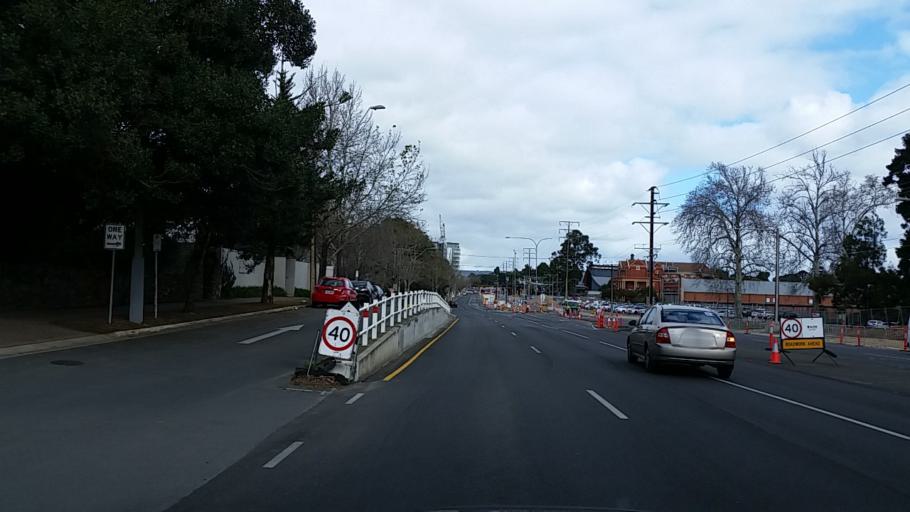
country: AU
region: South Australia
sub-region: Adelaide
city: Adelaide
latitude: -34.9149
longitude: 138.6141
